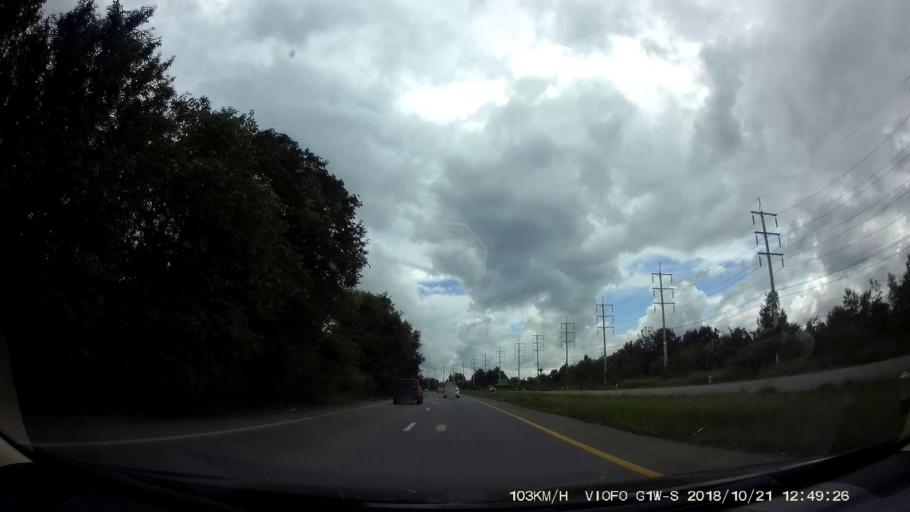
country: TH
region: Nakhon Ratchasima
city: Amphoe Sikhiu
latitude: 14.8965
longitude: 101.6844
